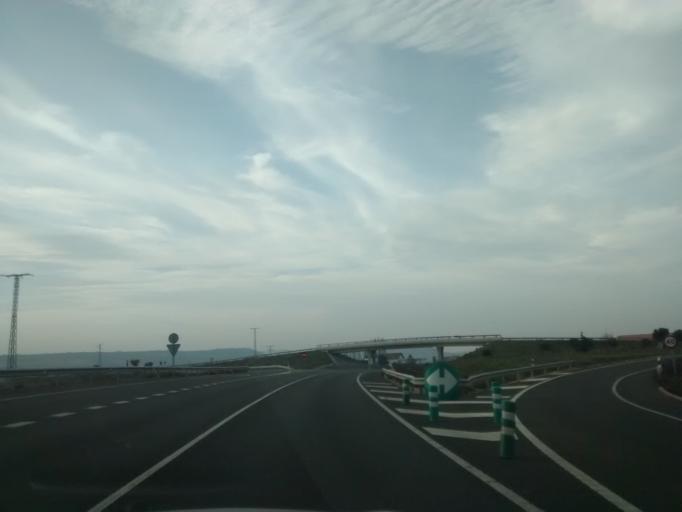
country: ES
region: La Rioja
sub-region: Provincia de La Rioja
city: San Asensio
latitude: 42.5120
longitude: -2.7376
